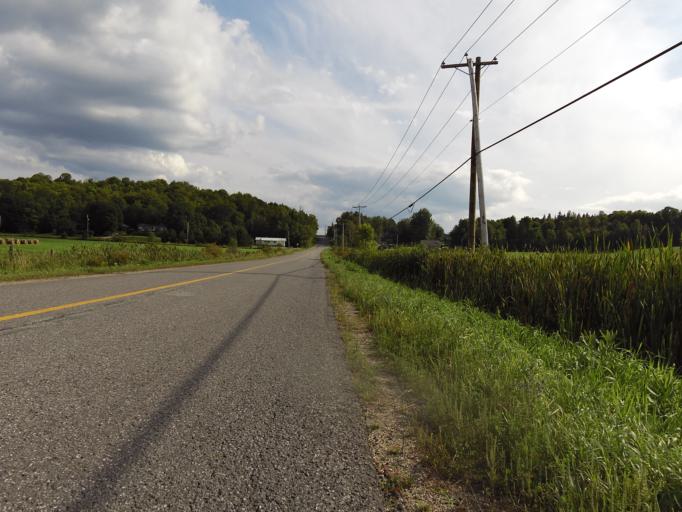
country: CA
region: Quebec
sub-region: Outaouais
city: Wakefield
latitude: 45.6549
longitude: -76.0167
